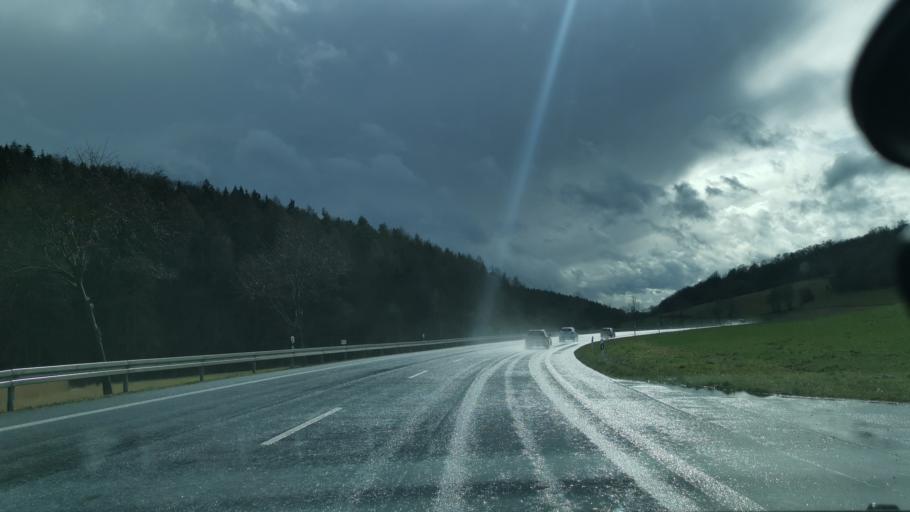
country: DE
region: Hesse
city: Bebra
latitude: 51.0011
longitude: 9.8142
